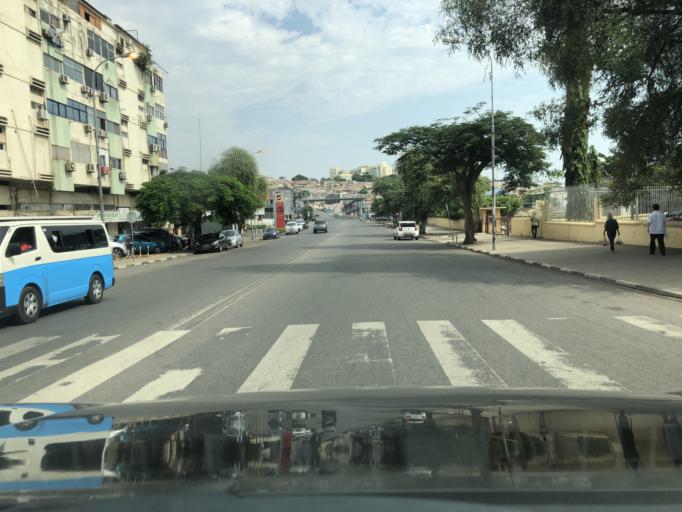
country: AO
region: Luanda
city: Luanda
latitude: -8.8277
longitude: 13.2267
